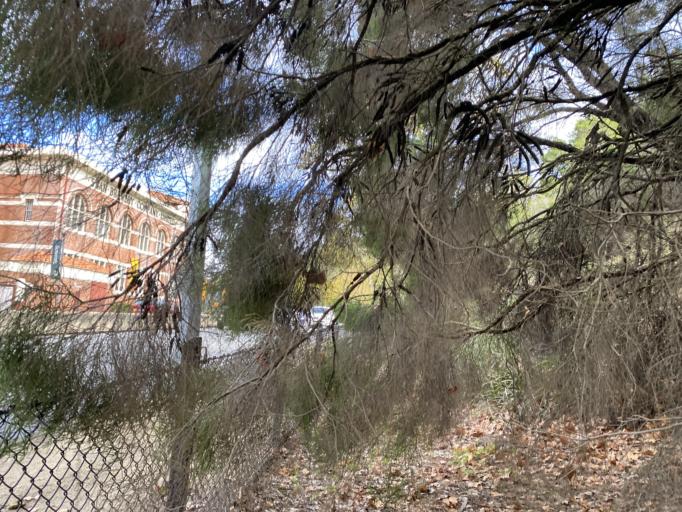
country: AU
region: Western Australia
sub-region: City of Perth
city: West Perth
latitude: -31.9644
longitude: 115.8409
